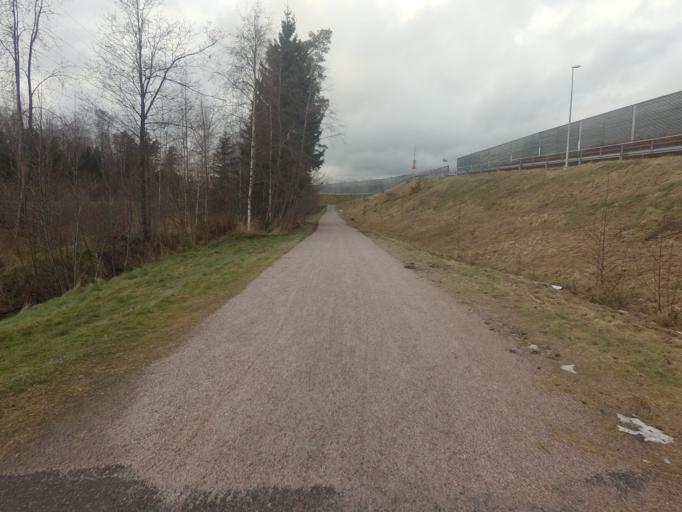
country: FI
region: Uusimaa
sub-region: Helsinki
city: Otaniemi
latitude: 60.2072
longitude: 24.8138
